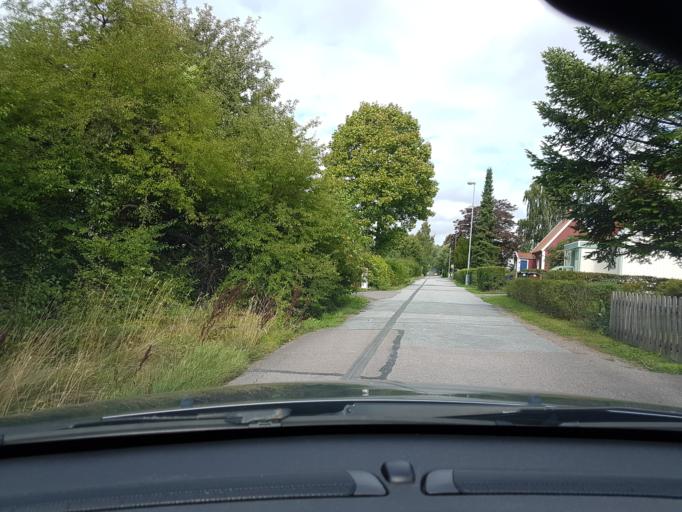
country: SE
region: Vaestra Goetaland
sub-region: Ale Kommun
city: Nodinge-Nol
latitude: 57.9164
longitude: 12.0680
